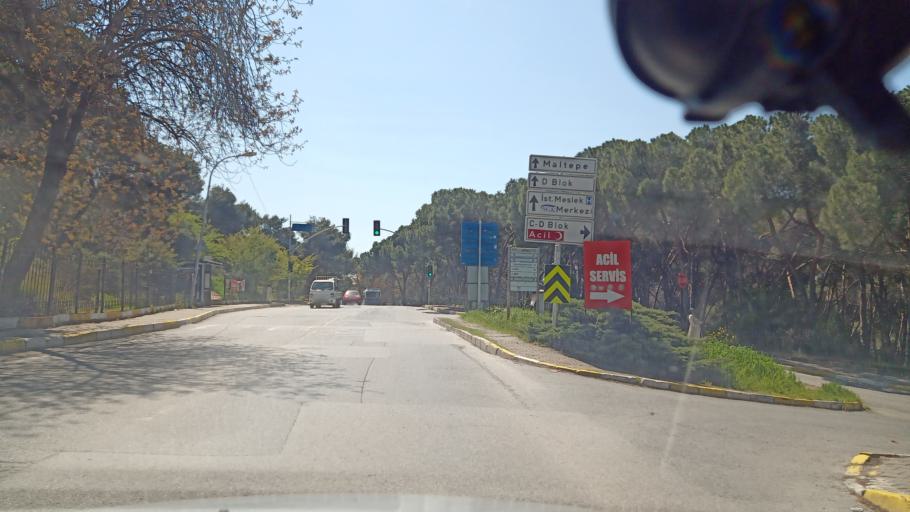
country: TR
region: Istanbul
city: Maltepe
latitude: 40.9509
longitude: 29.1423
